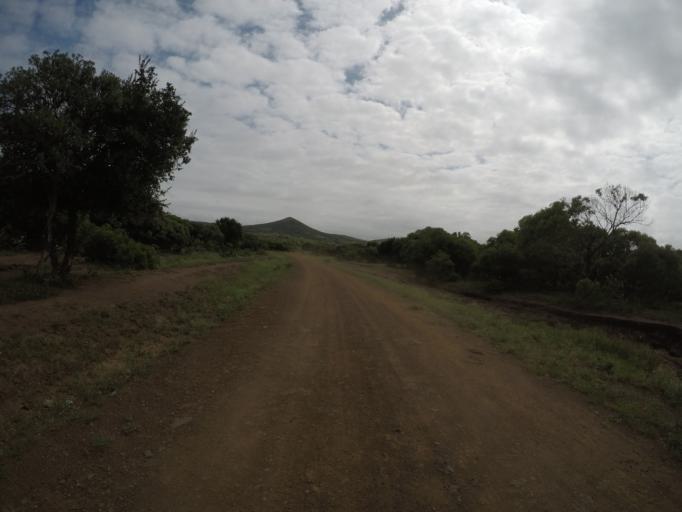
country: ZA
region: KwaZulu-Natal
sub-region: uThungulu District Municipality
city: Empangeni
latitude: -28.6220
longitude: 31.8559
